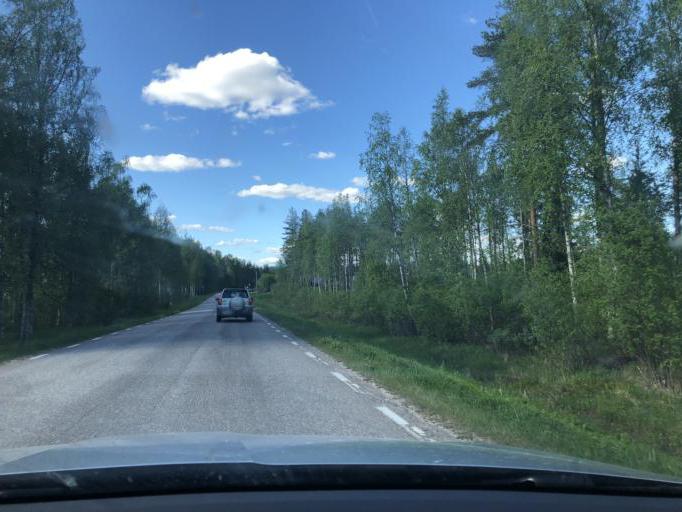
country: SE
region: Norrbotten
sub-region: Kalix Kommun
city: Kalix
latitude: 65.9278
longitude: 23.1625
